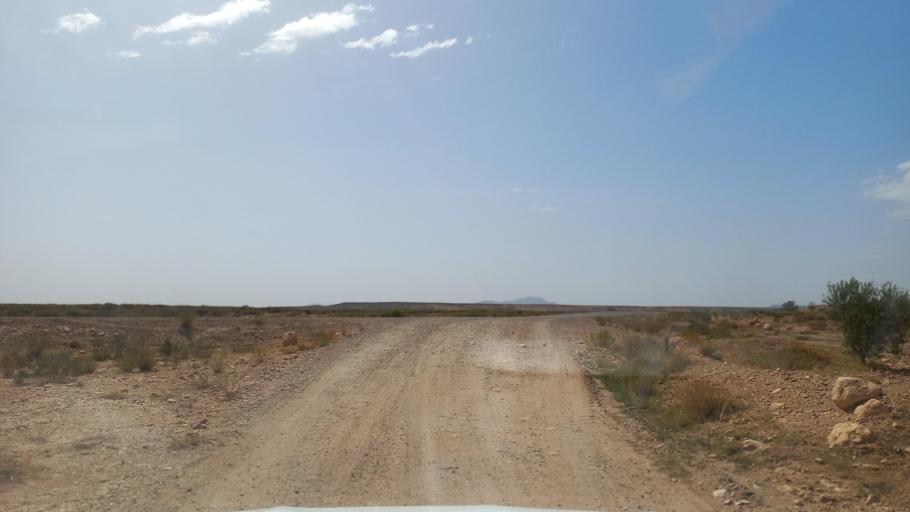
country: TN
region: Al Qasrayn
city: Kasserine
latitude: 35.2534
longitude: 8.9571
